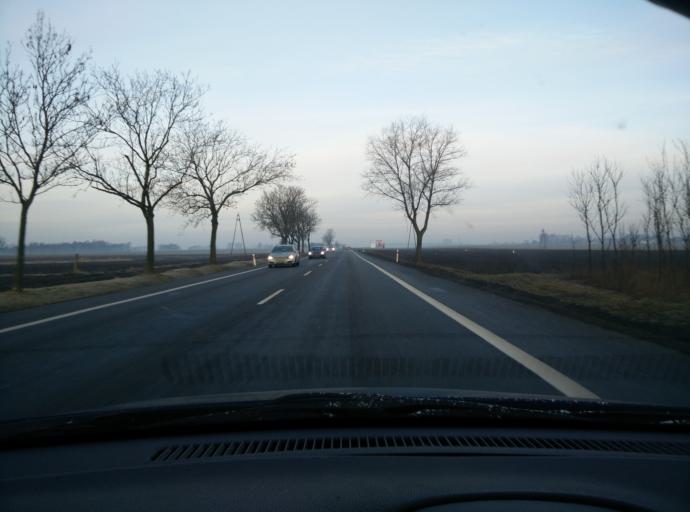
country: PL
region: Greater Poland Voivodeship
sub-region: Powiat poznanski
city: Kornik
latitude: 52.2393
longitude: 17.1531
